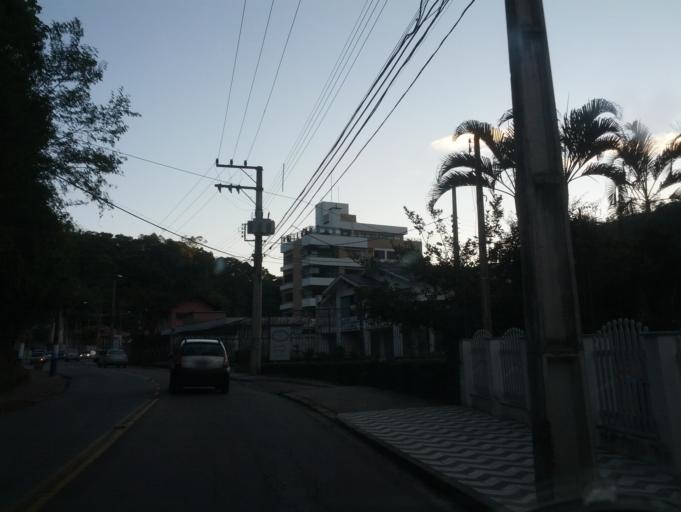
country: BR
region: Santa Catarina
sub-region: Blumenau
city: Blumenau
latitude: -26.9254
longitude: -49.0725
